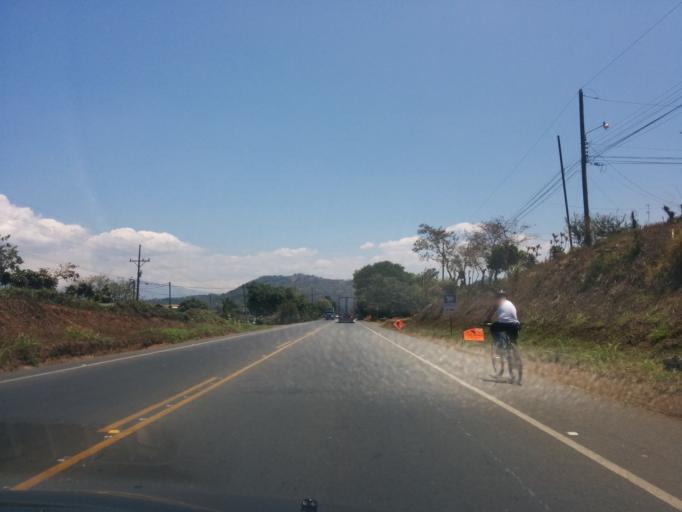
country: CR
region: Alajuela
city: San Ramon
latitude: 10.0763
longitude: -84.4738
